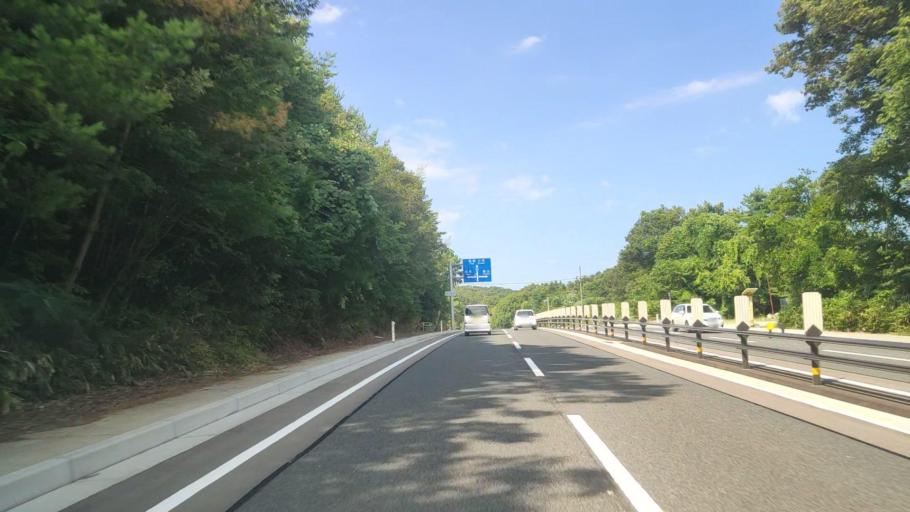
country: JP
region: Ishikawa
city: Matsuto
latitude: 36.4327
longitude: 136.5389
